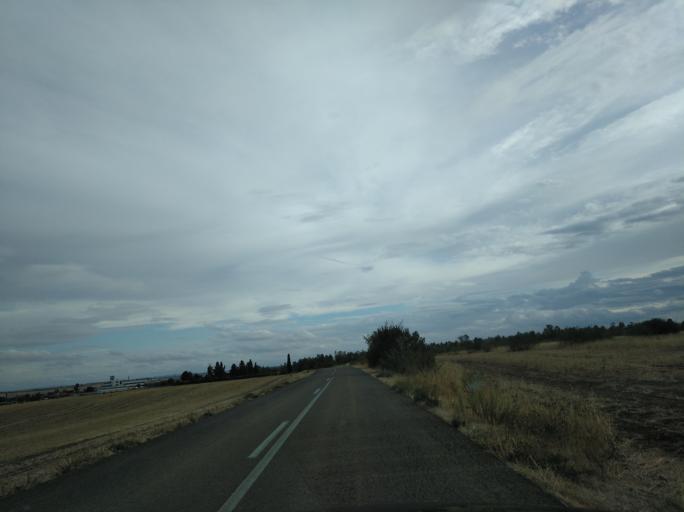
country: ES
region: Extremadura
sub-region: Provincia de Badajoz
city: Badajoz
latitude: 38.8957
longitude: -7.0170
